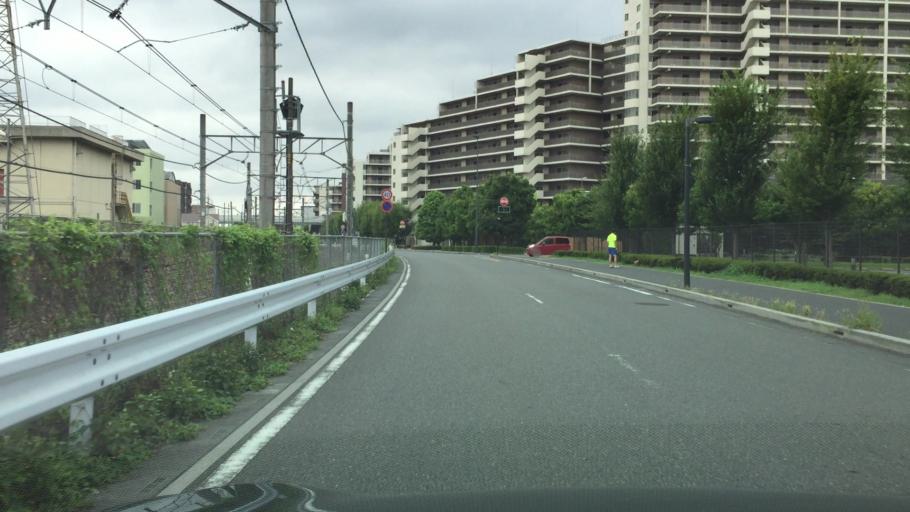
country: JP
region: Saitama
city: Ageoshimo
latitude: 35.9367
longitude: 139.6102
